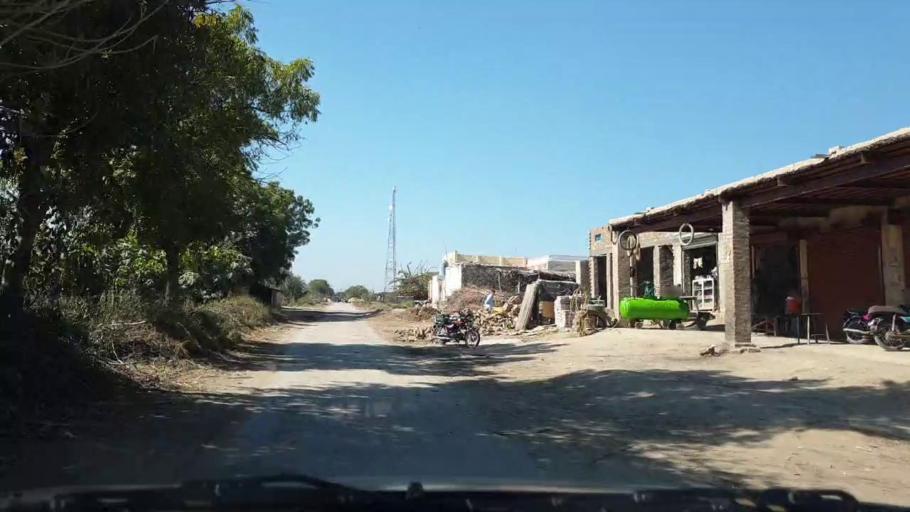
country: PK
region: Sindh
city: Khadro
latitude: 26.1288
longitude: 68.8061
